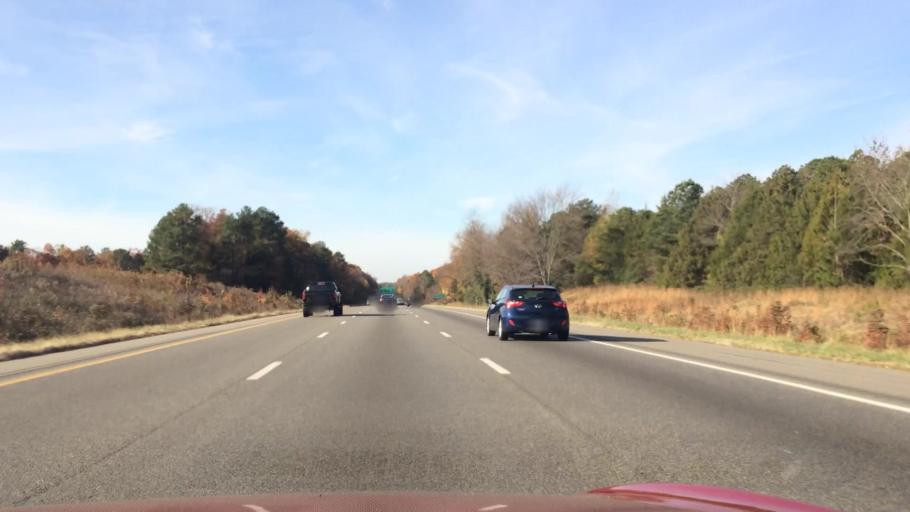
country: US
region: Virginia
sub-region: Henrico County
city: Wyndham
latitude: 37.6771
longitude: -77.5626
